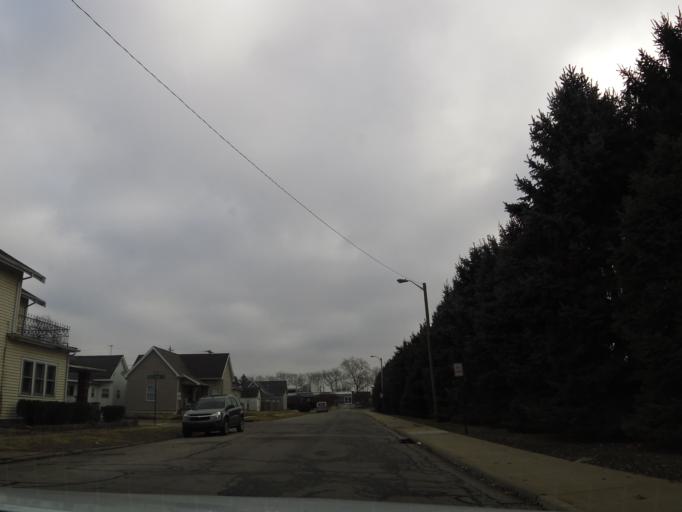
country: US
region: Indiana
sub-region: Bartholomew County
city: Columbus
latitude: 39.2047
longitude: -85.9073
